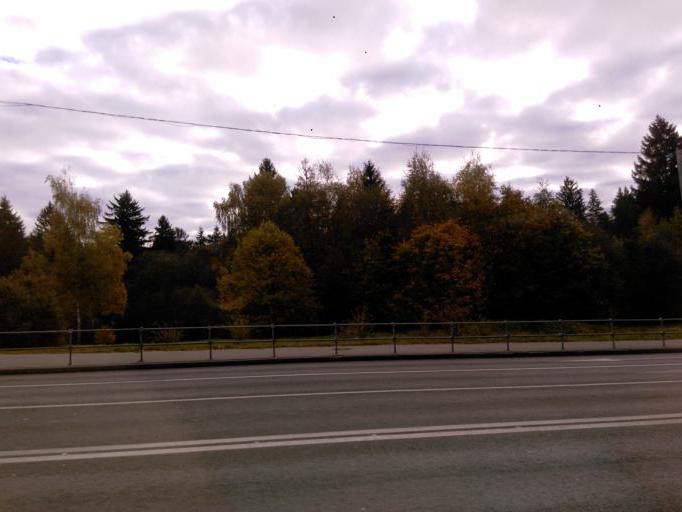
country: RU
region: Moscow
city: Zelenograd
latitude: 55.9917
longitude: 37.1861
